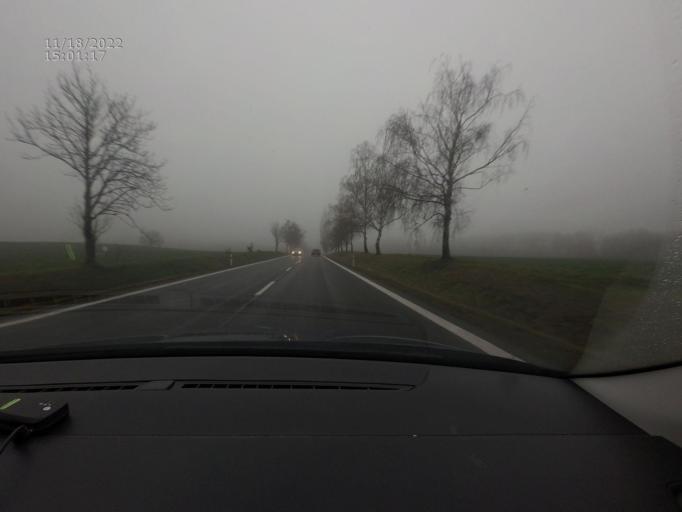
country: CZ
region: Jihocesky
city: Kovarov
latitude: 49.5048
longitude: 14.2079
